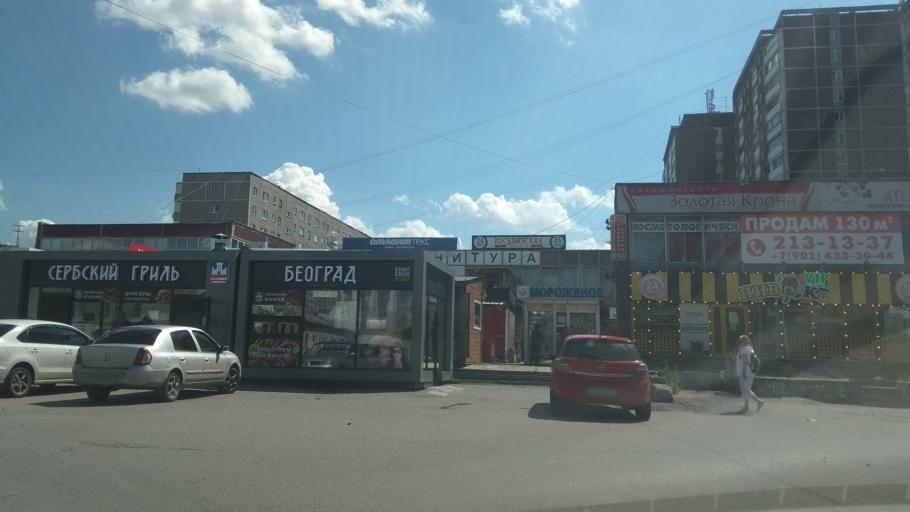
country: RU
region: Sverdlovsk
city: Yekaterinburg
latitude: 56.8348
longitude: 60.6885
